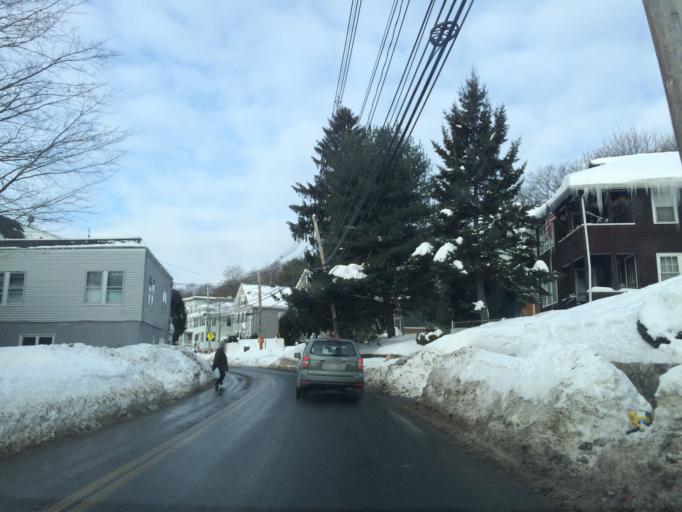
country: US
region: Massachusetts
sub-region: Middlesex County
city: Waltham
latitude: 42.3787
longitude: -71.2477
